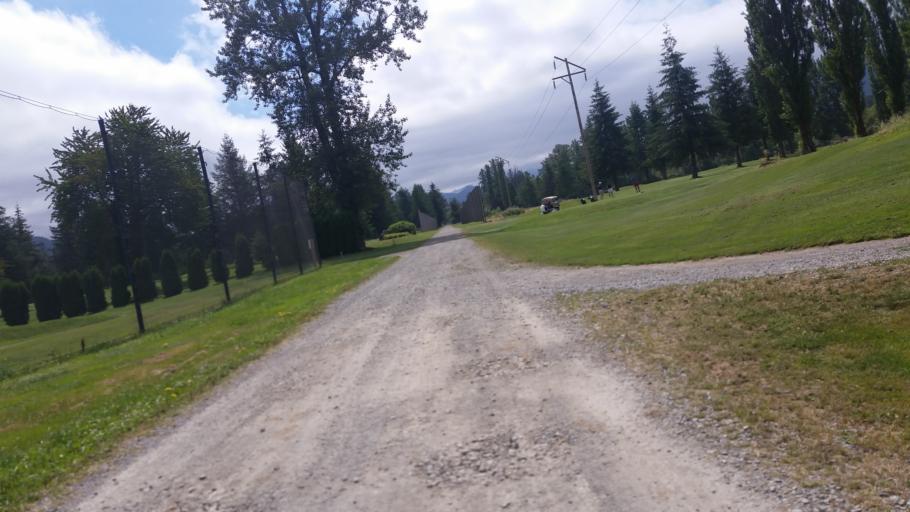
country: US
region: Washington
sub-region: King County
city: North Bend
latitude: 47.5165
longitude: -121.7971
